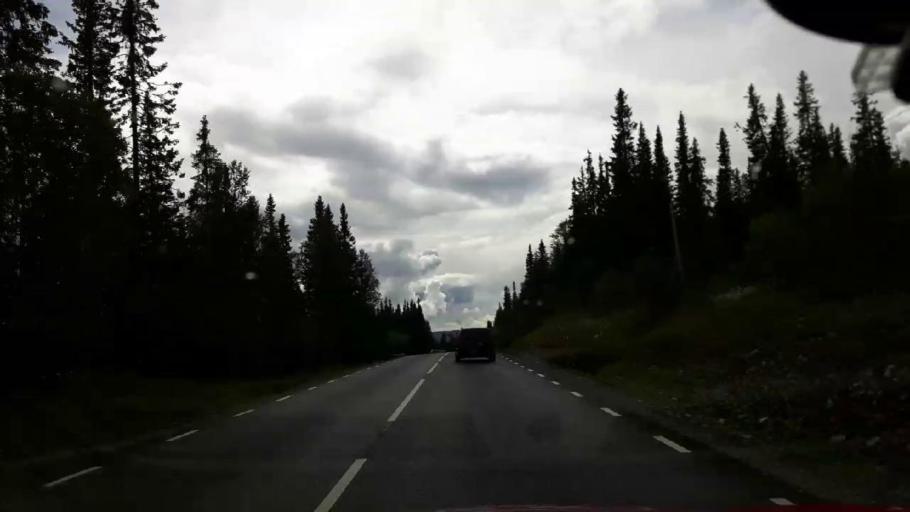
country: NO
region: Nord-Trondelag
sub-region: Royrvik
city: Royrvik
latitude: 64.8356
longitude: 14.1269
